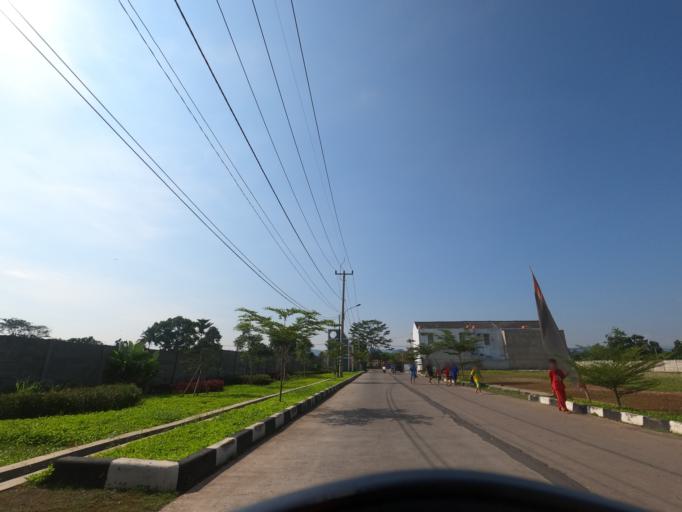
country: ID
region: West Java
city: Lembang
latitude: -6.5769
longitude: 107.7912
